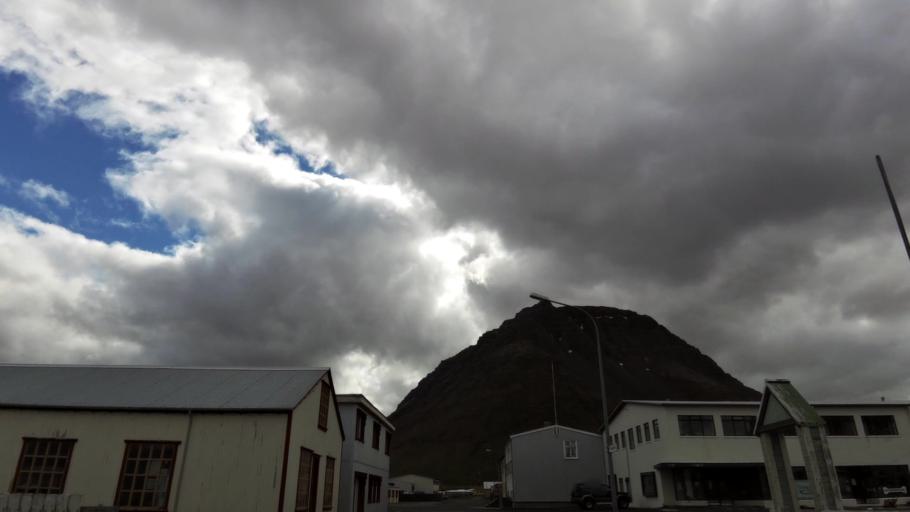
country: IS
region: Westfjords
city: Isafjoerdur
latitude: 66.1576
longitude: -23.2478
